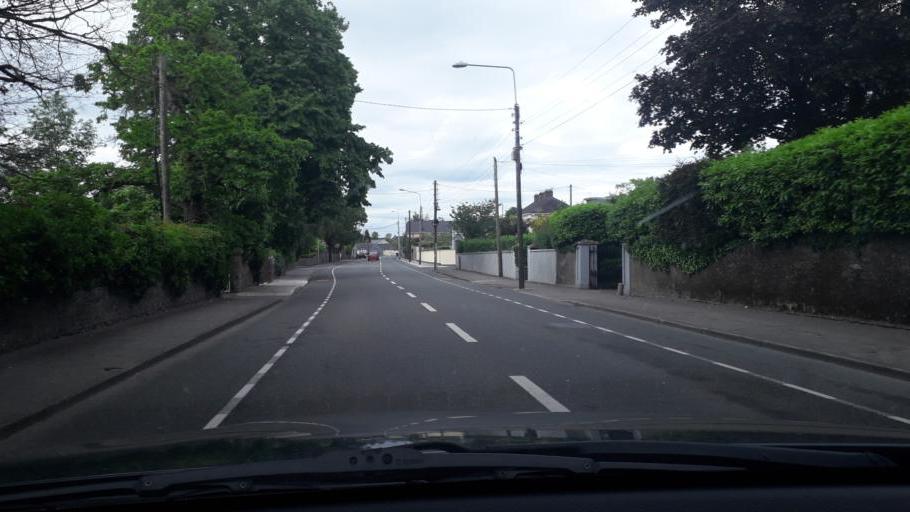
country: IE
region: Leinster
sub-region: County Carlow
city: Carlow
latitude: 52.8315
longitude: -6.9347
